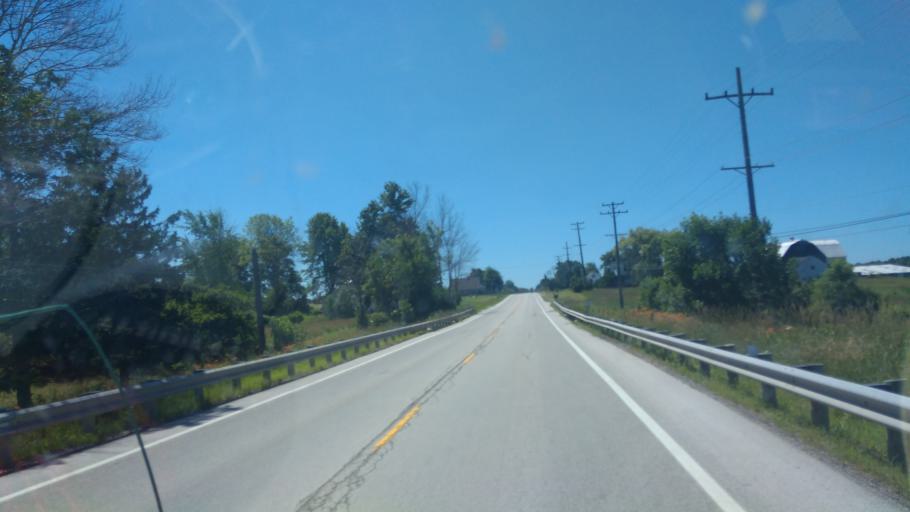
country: US
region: Ohio
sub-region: Ashtabula County
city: Conneaut
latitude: 41.8608
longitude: -80.5725
